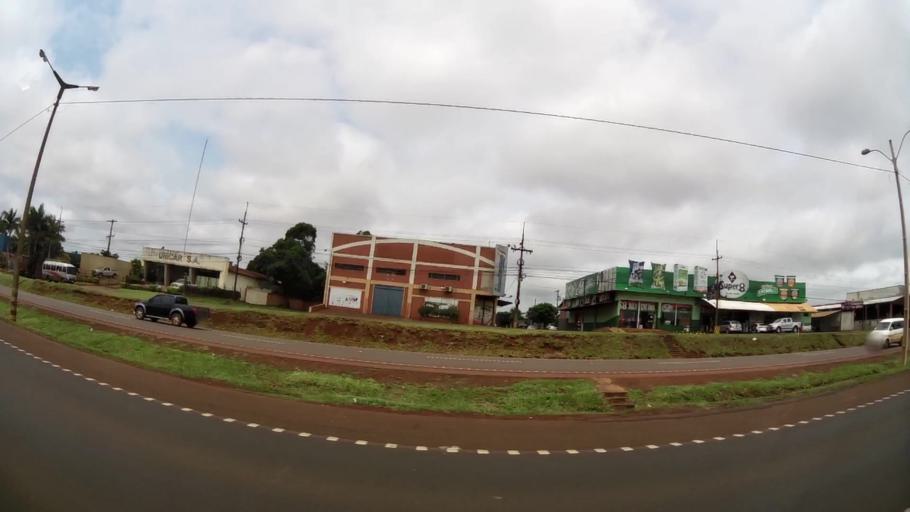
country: PY
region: Alto Parana
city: Ciudad del Este
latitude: -25.4960
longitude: -54.6833
